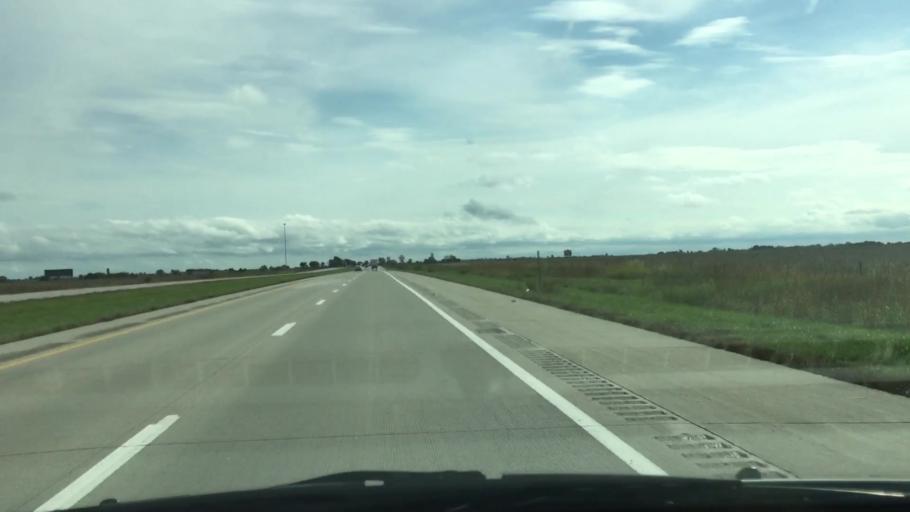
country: US
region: Iowa
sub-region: Clarke County
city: Osceola
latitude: 40.9389
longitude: -93.7993
